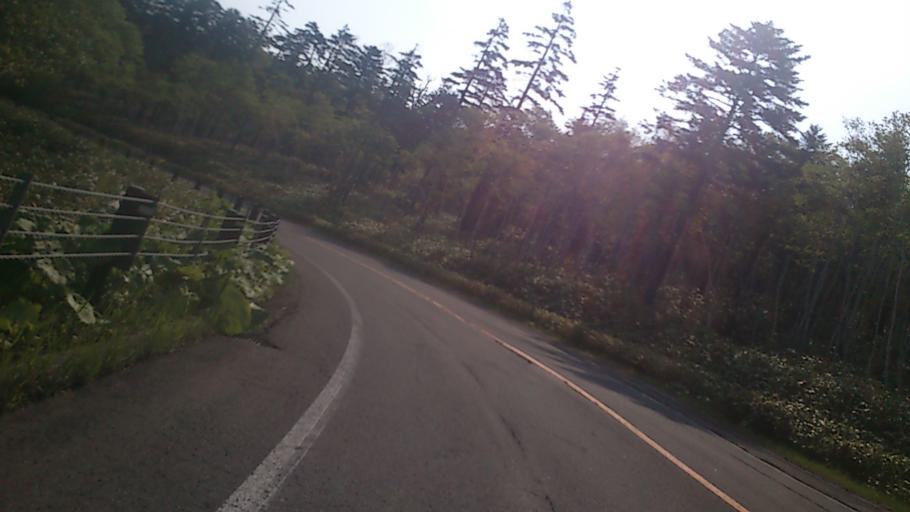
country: JP
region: Hokkaido
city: Bihoro
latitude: 43.4493
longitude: 144.2228
